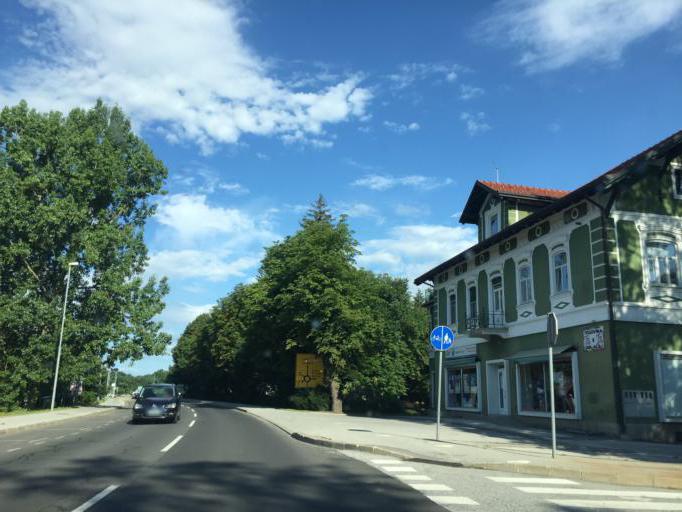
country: SI
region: Radenci
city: Radenci
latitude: 46.6416
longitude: 16.0425
